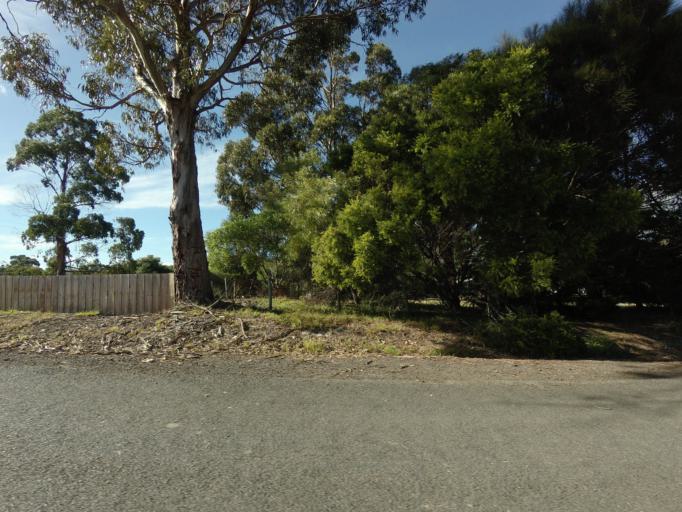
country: AU
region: Tasmania
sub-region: Clarence
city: Sandford
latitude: -42.9962
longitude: 147.7102
